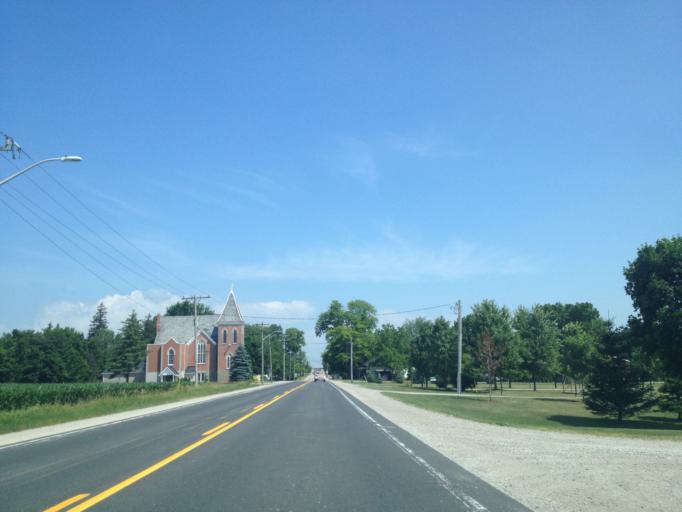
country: CA
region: Ontario
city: Huron East
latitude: 43.3875
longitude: -81.2214
